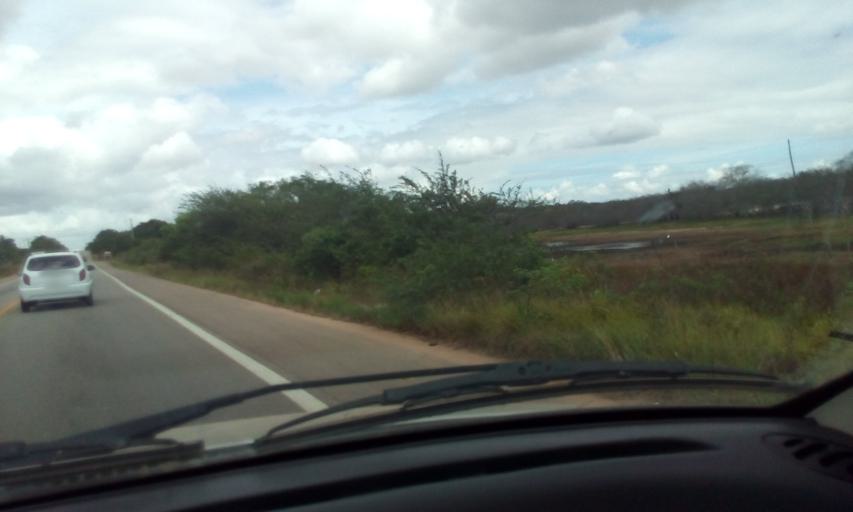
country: BR
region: Rio Grande do Norte
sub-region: Macaiba
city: Macaiba
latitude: -5.9309
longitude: -35.5432
